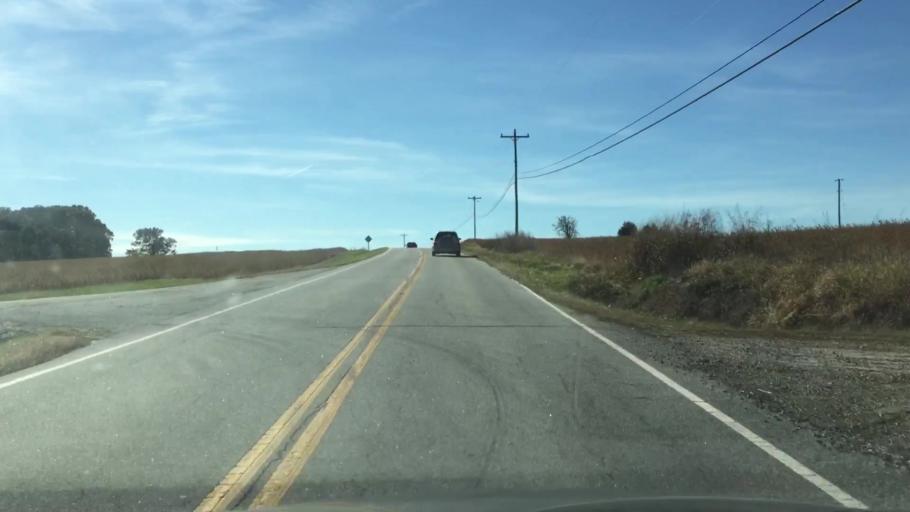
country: US
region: North Carolina
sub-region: Rowan County
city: China Grove
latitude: 35.6399
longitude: -80.6590
